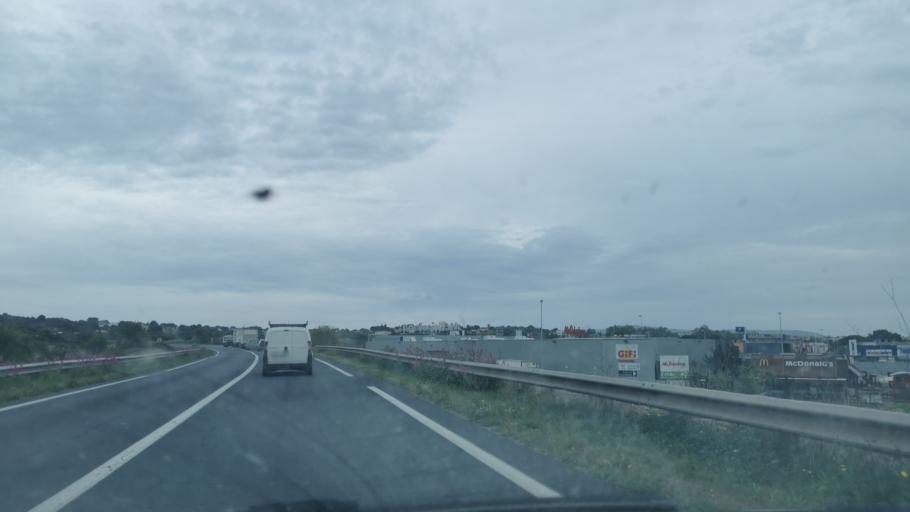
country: FR
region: Languedoc-Roussillon
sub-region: Departement de l'Herault
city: Balaruc-le-Vieux
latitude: 43.4617
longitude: 3.6935
